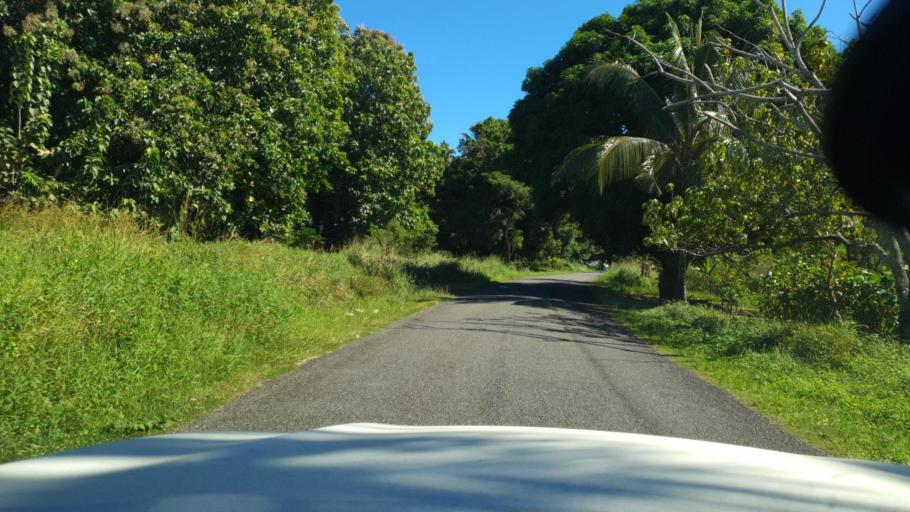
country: SB
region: Guadalcanal
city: Honiara
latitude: -9.2633
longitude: 159.7272
